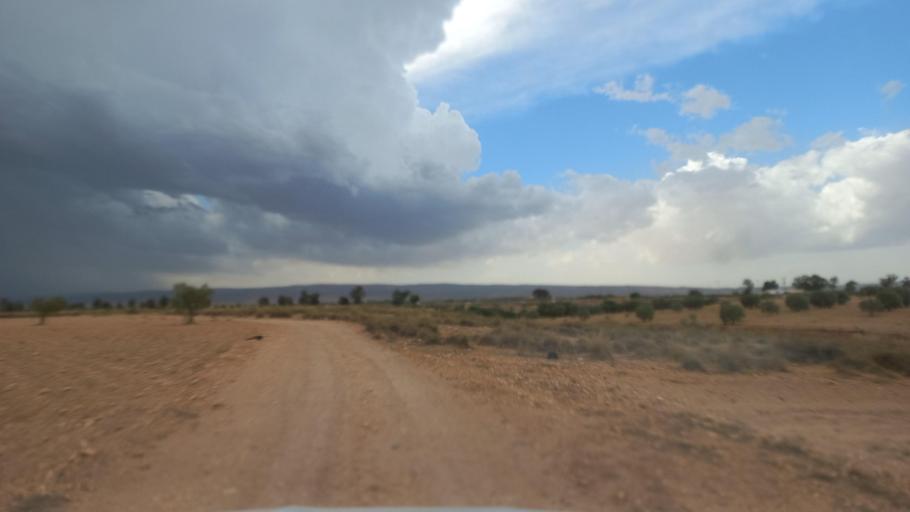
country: TN
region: Al Qasrayn
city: Kasserine
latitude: 35.2459
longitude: 9.0063
